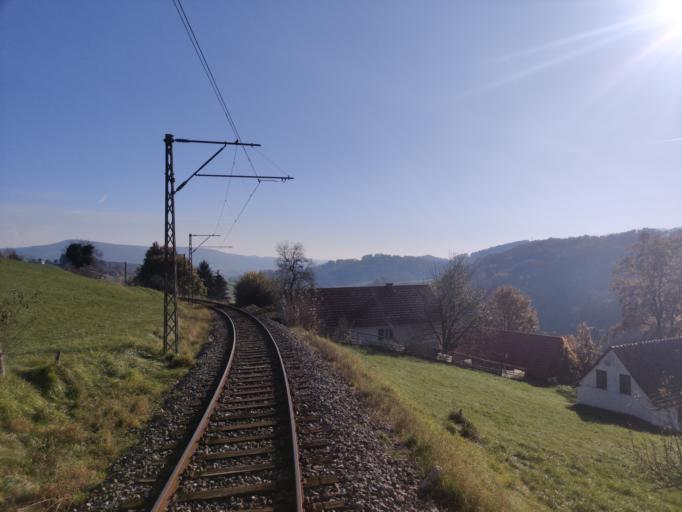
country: AT
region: Styria
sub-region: Politischer Bezirk Suedoststeiermark
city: Trautmannsdorf in Oststeiermark
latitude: 46.8889
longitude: 15.8754
